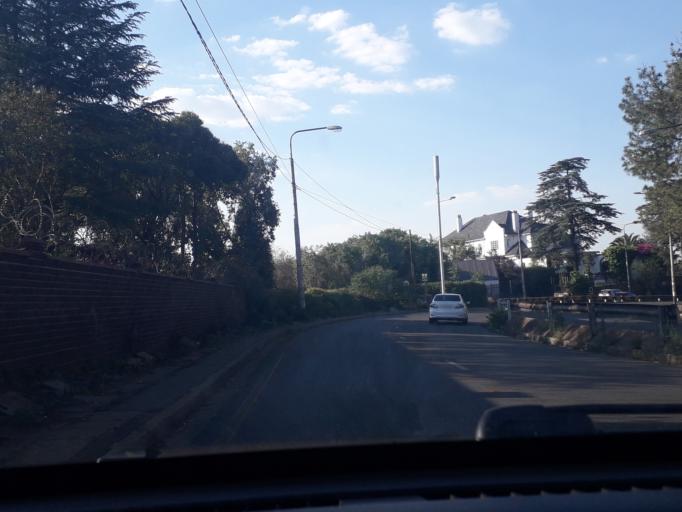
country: ZA
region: Gauteng
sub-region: City of Johannesburg Metropolitan Municipality
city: Johannesburg
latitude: -26.1786
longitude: 28.0297
